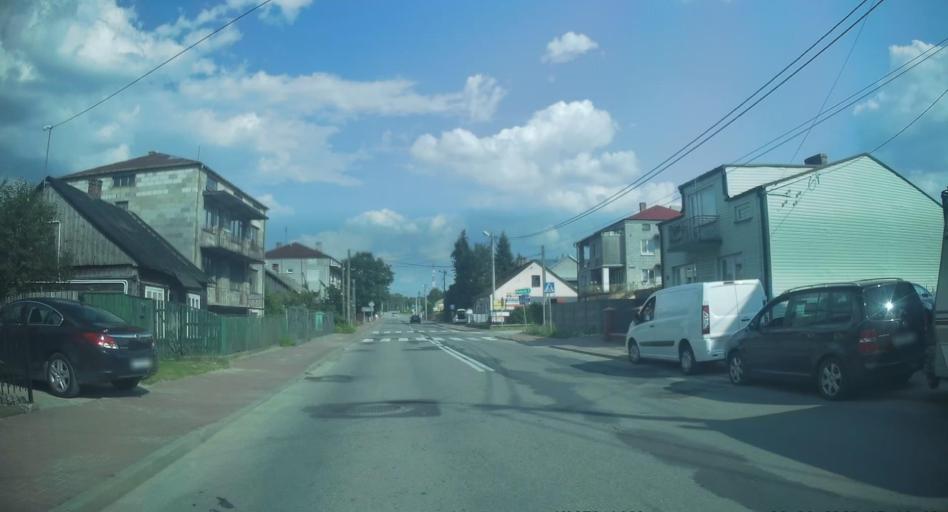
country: PL
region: Swietokrzyskie
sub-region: Powiat konecki
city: Radoszyce
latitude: 51.0726
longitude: 20.2638
